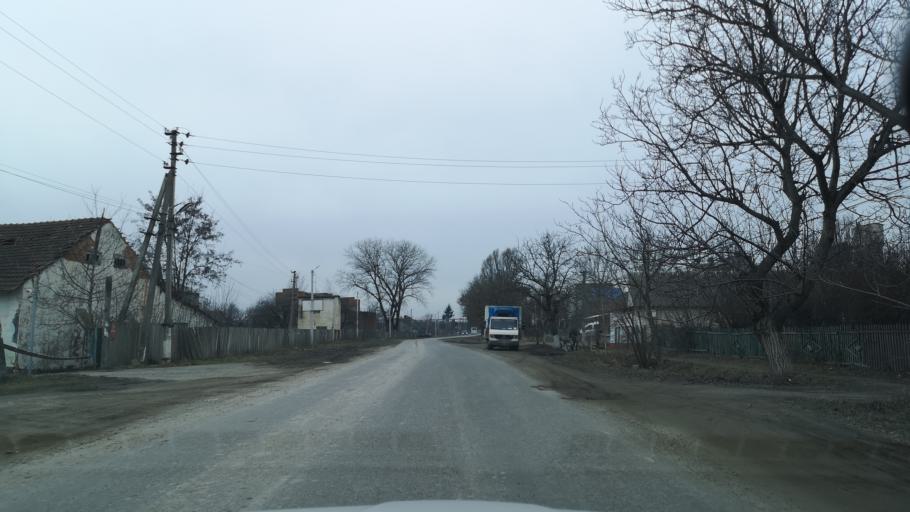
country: RO
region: Botosani
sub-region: Comuna Darabani
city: Bajura
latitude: 48.2535
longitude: 26.5726
